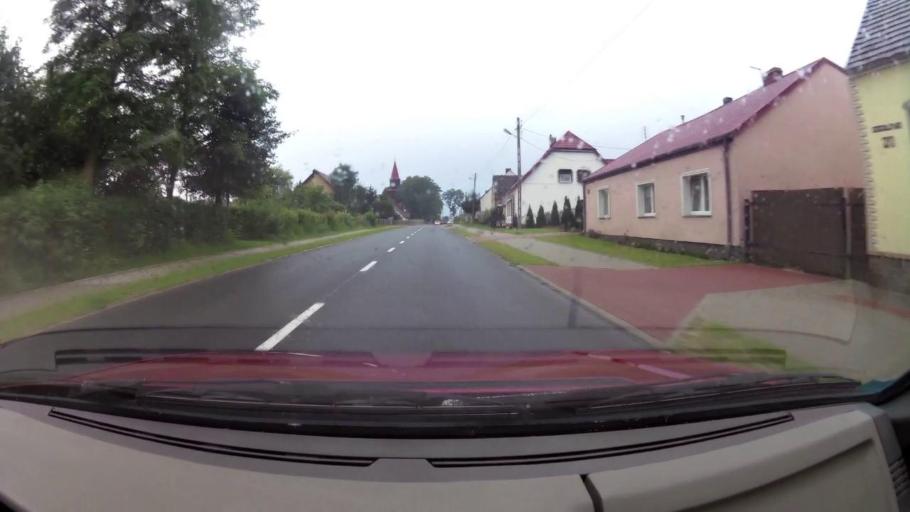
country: PL
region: West Pomeranian Voivodeship
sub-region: Powiat stargardzki
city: Stara Dabrowa
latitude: 53.3818
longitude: 15.1701
